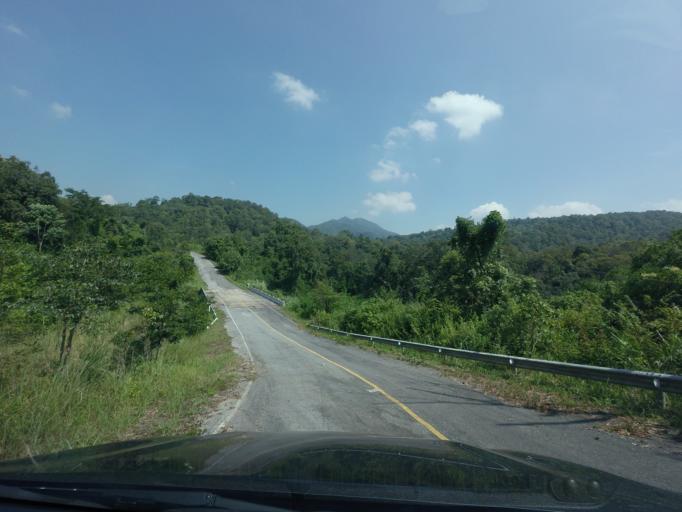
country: TH
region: Loei
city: Na Haeo
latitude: 17.5727
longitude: 100.9647
